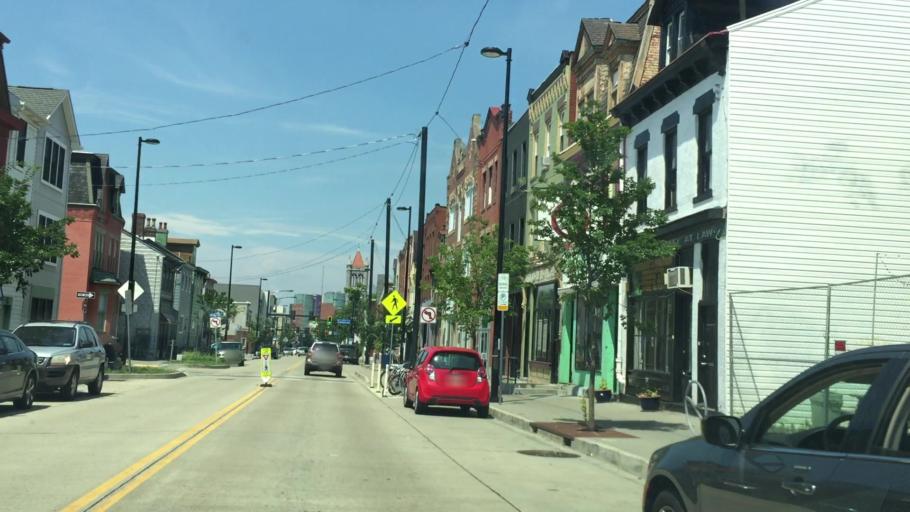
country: US
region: Pennsylvania
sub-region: Allegheny County
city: Bloomfield
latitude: 40.4651
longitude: -79.9436
